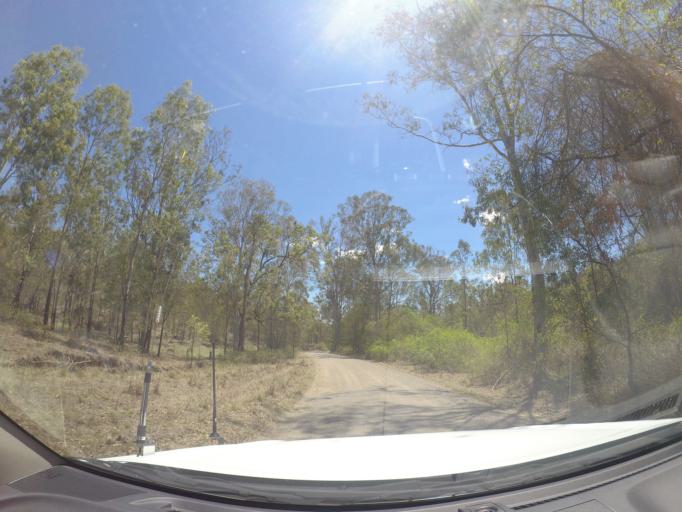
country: AU
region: Queensland
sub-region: Ipswich
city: Redbank Plains
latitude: -27.7576
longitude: 152.8366
